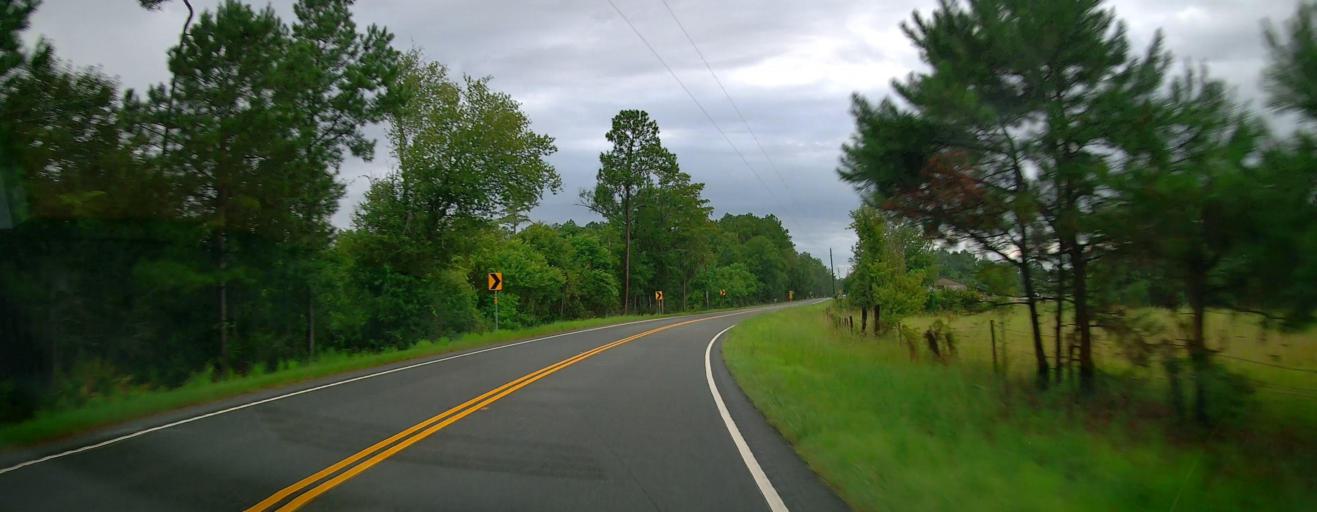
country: US
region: Georgia
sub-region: Ware County
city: Deenwood
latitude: 31.2725
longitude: -82.4133
